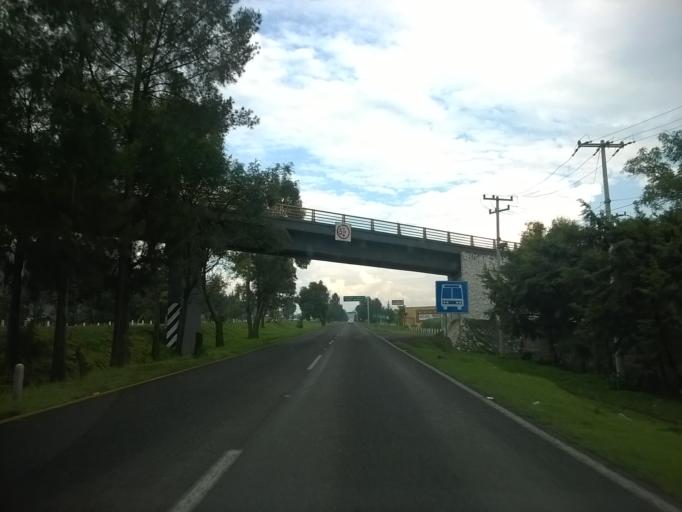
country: MX
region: Michoacan
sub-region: Huiramba
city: El Pedregal
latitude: 19.5321
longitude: -101.4916
